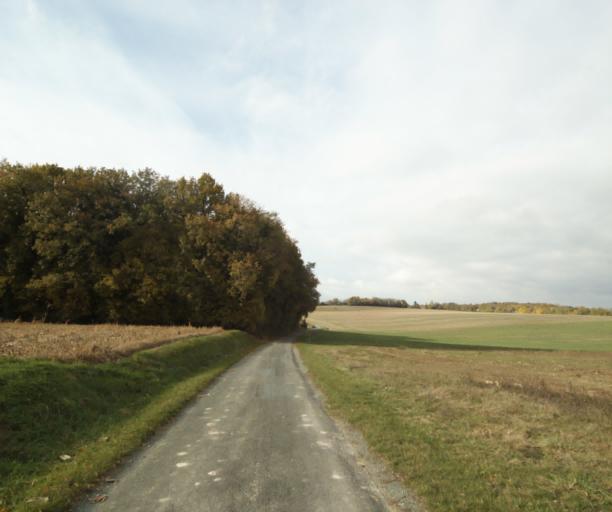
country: FR
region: Poitou-Charentes
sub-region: Departement de la Charente-Maritime
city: Saint-Georges-des-Coteaux
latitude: 45.7614
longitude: -0.6765
